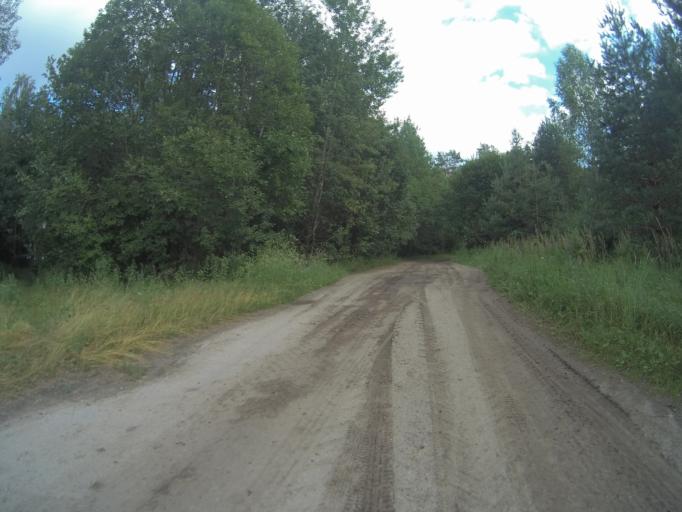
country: RU
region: Vladimir
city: Raduzhnyy
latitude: 56.0028
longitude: 40.2102
